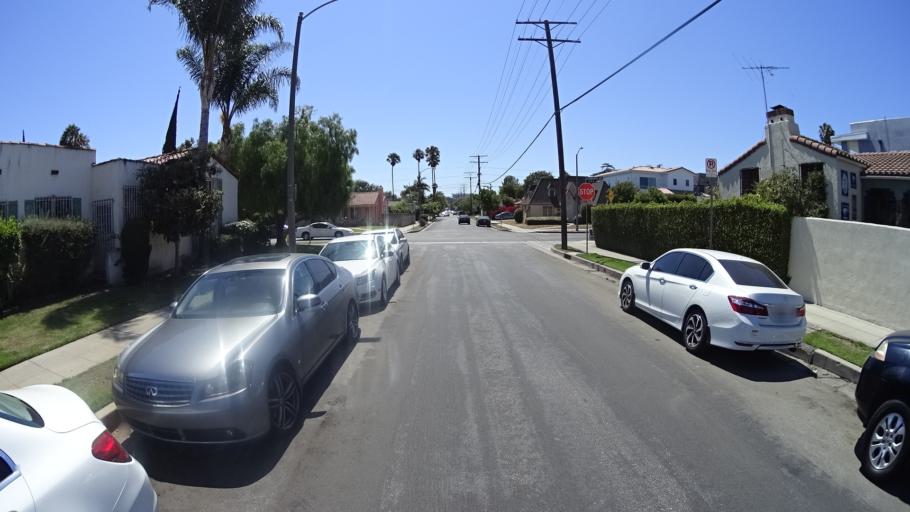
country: US
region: California
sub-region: Los Angeles County
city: West Hollywood
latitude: 34.0744
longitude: -118.3633
